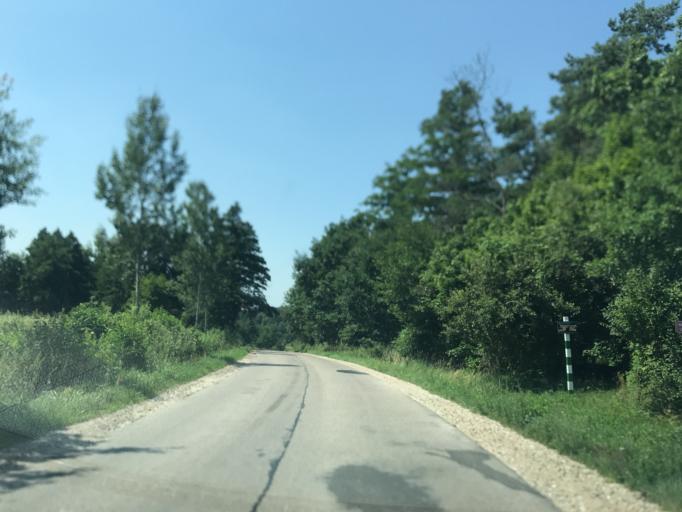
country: PL
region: Kujawsko-Pomorskie
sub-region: Powiat lipnowski
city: Chrostkowo
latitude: 52.9841
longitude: 19.3073
